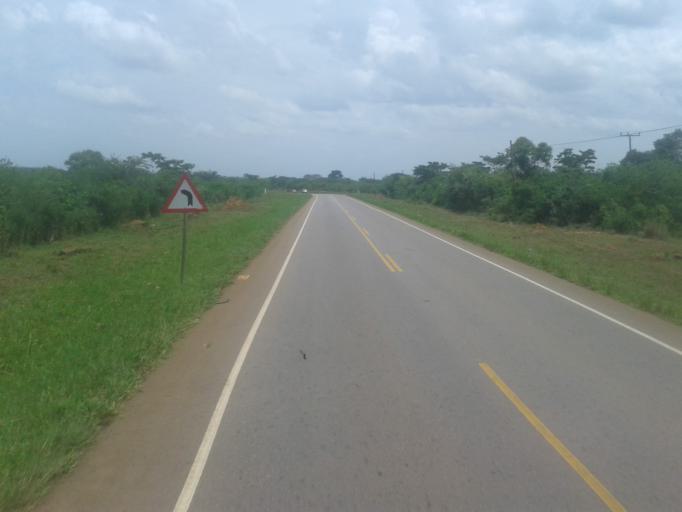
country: UG
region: Central Region
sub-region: Nakasongola District
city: Nakasongola
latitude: 1.3962
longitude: 32.3158
